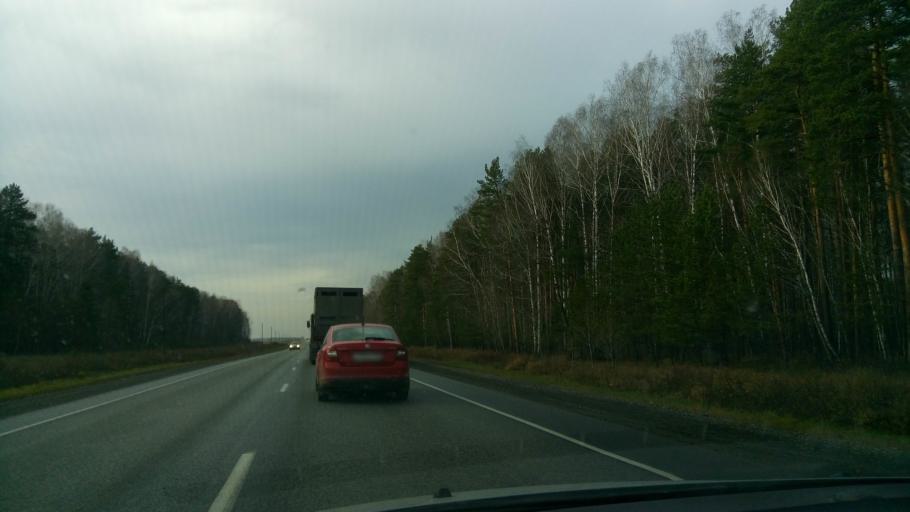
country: RU
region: Sverdlovsk
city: Gryaznovskoye
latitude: 56.7829
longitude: 61.6365
